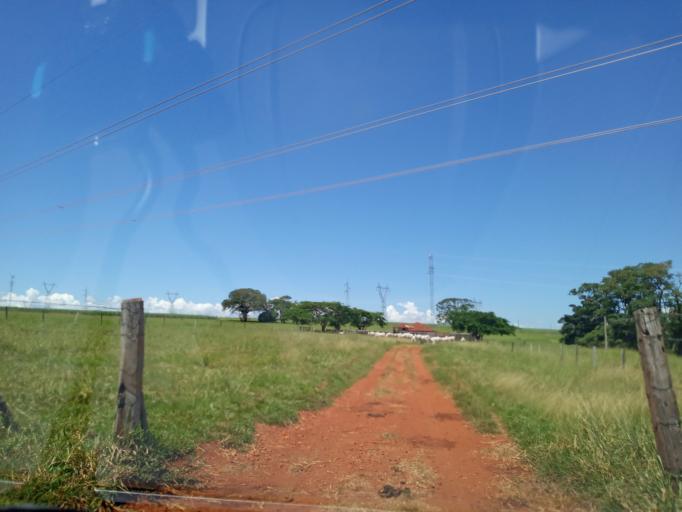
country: BR
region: Goias
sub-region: Itumbiara
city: Itumbiara
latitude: -18.3957
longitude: -49.1249
